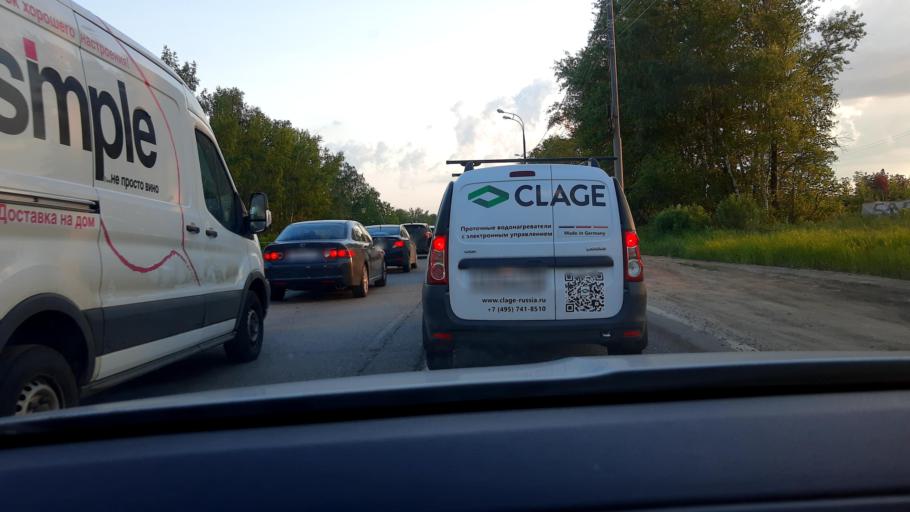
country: RU
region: Moskovskaya
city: Nazar'yevo
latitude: 55.6379
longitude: 37.0474
